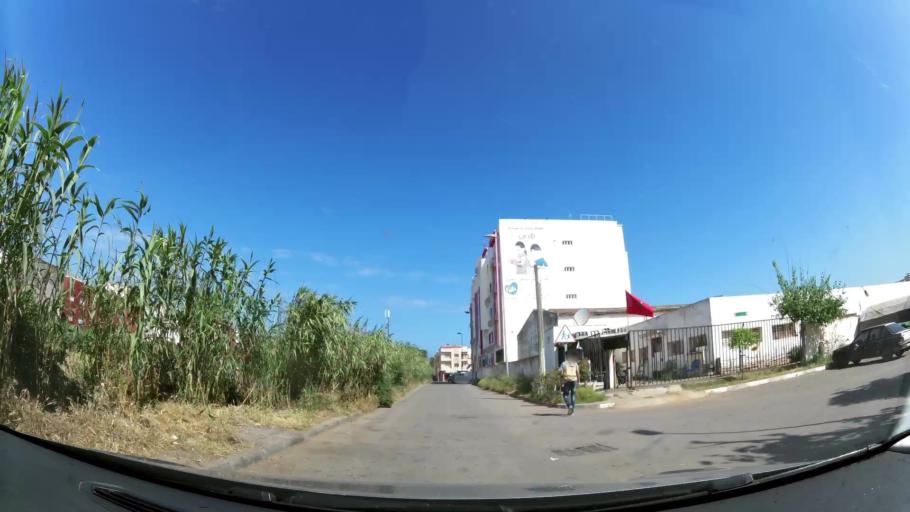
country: MA
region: Rabat-Sale-Zemmour-Zaer
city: Sale
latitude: 34.0623
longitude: -6.8022
